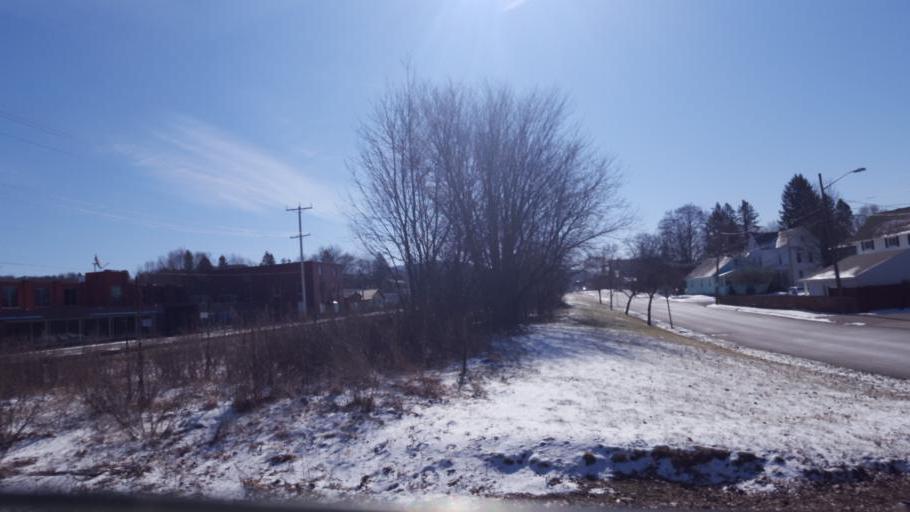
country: US
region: New York
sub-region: Allegany County
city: Wellsville
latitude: 42.1266
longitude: -77.9520
